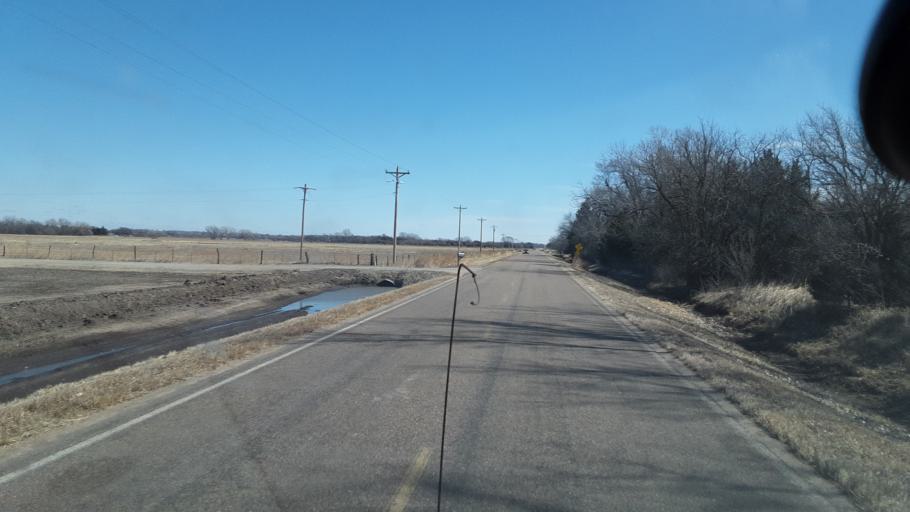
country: US
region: Kansas
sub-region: Reno County
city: Nickerson
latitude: 38.2174
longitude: -98.0790
